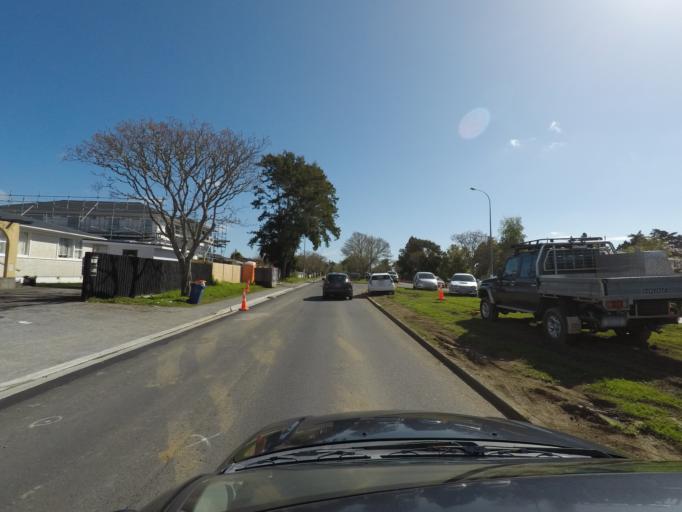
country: NZ
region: Auckland
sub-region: Auckland
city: Rosebank
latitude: -36.8575
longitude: 174.6187
